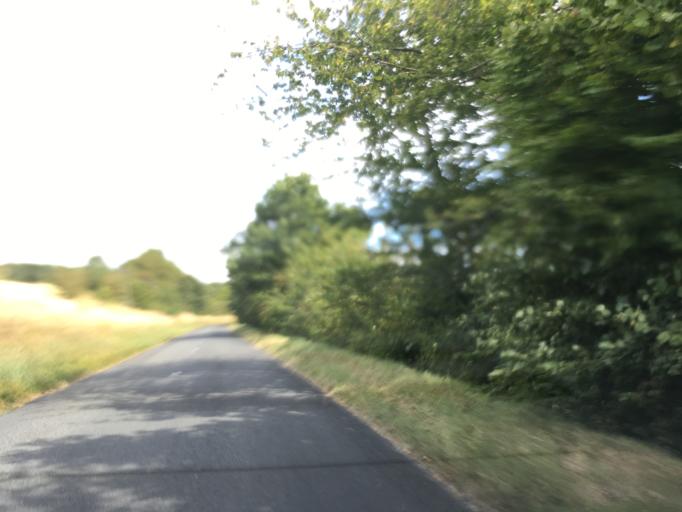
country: FR
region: Haute-Normandie
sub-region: Departement de l'Eure
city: Heudreville-sur-Eure
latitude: 49.1327
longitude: 1.2208
